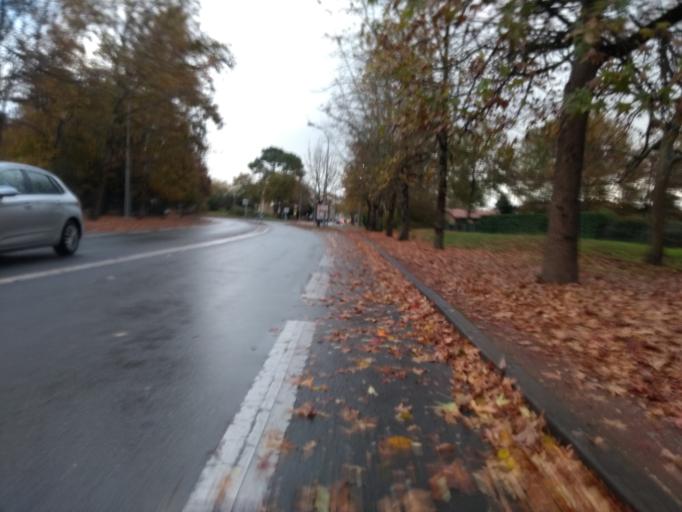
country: FR
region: Aquitaine
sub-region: Departement de la Gironde
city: Gradignan
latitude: 44.7744
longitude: -0.5862
